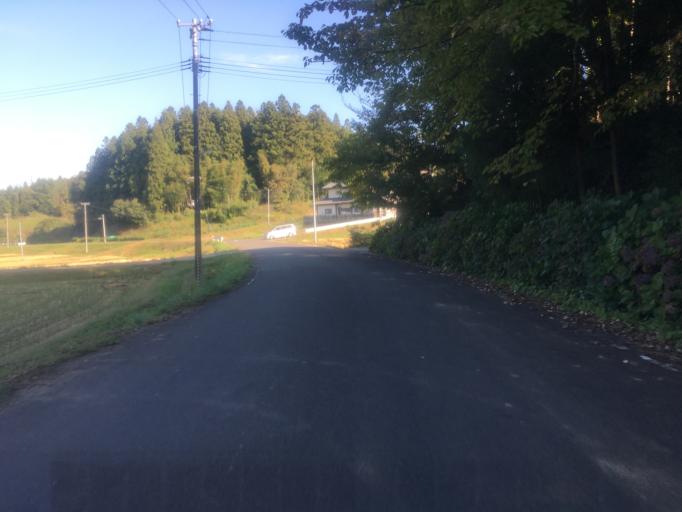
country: JP
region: Fukushima
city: Fukushima-shi
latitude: 37.6744
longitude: 140.4883
